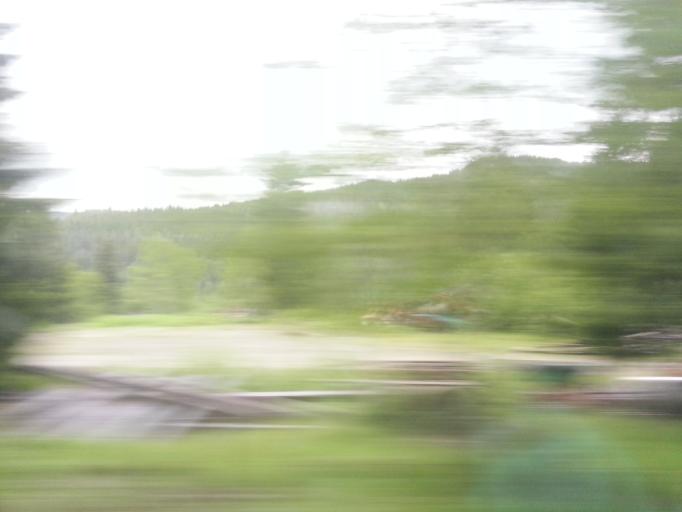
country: NO
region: Sor-Trondelag
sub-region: Midtre Gauldal
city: Storen
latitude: 62.9326
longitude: 10.1806
